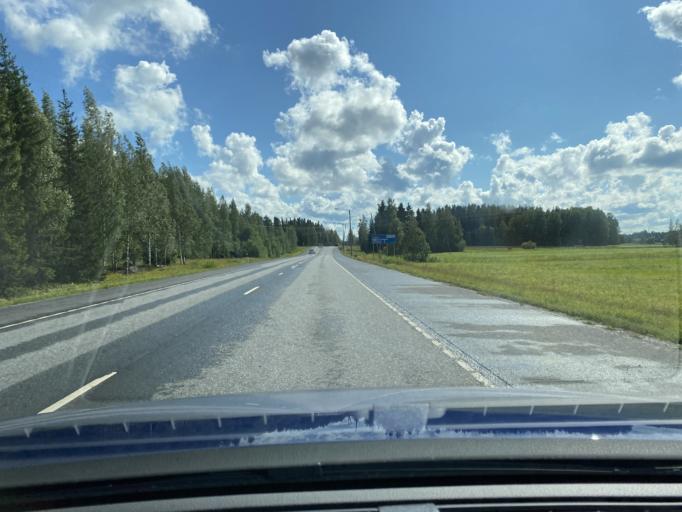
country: FI
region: Pirkanmaa
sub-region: Tampere
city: Lempaeaelae
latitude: 61.3291
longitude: 23.7758
